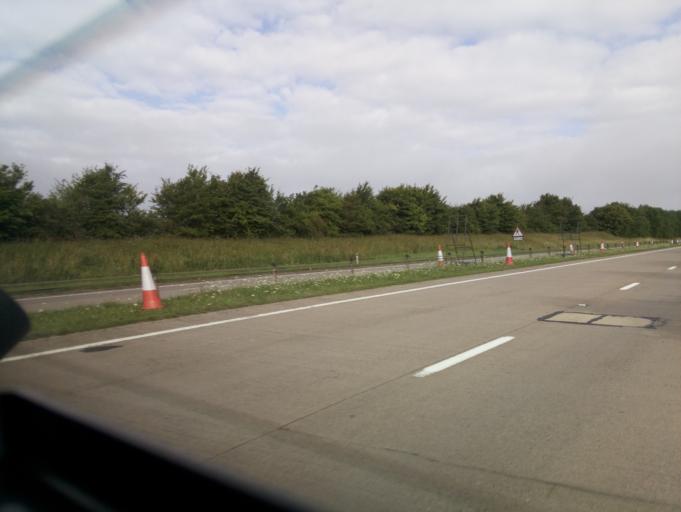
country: GB
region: England
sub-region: Gloucestershire
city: Cirencester
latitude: 51.7016
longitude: -1.9222
